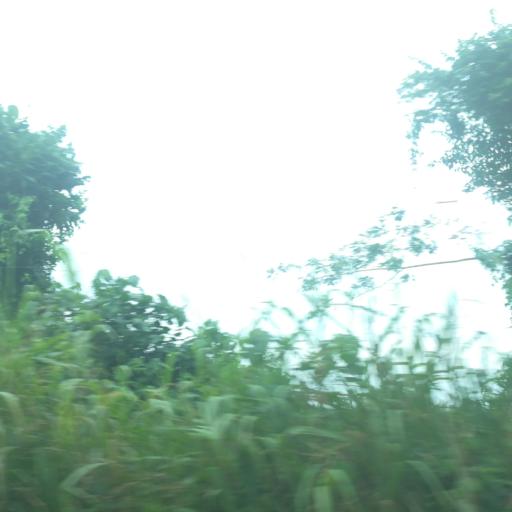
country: NG
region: Lagos
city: Ejirin
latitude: 6.6475
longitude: 3.7651
